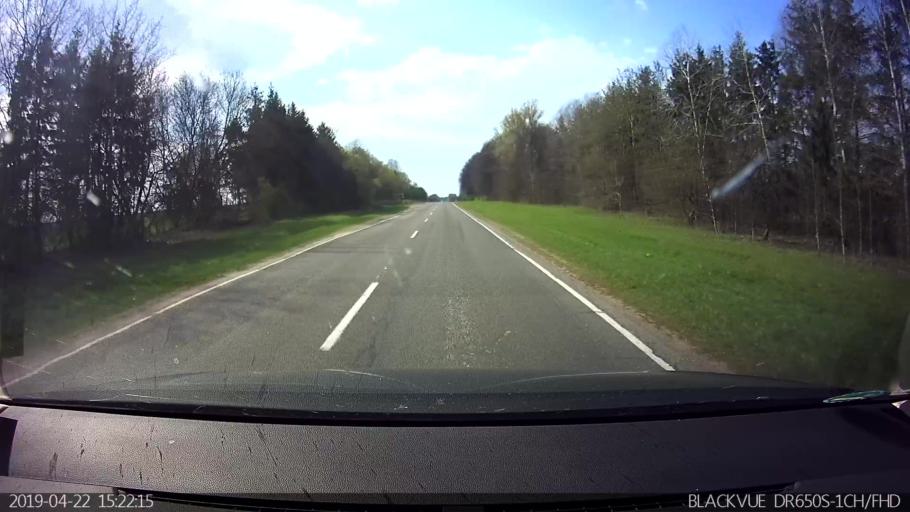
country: BY
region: Brest
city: Vysokaye
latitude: 52.3488
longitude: 23.4505
